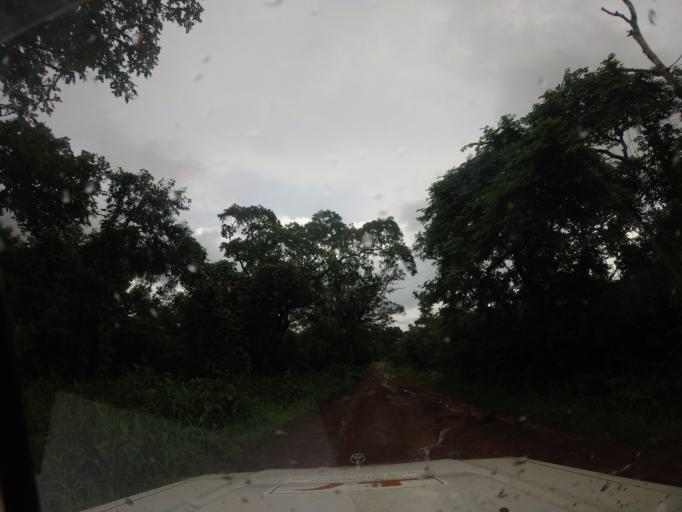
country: SL
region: Northern Province
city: Kamakwie
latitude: 9.7930
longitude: -12.3570
